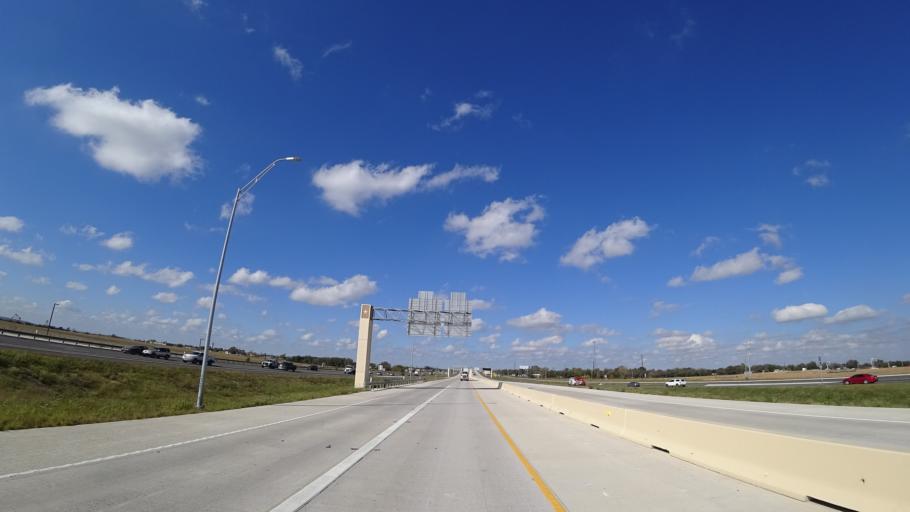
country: US
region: Texas
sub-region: Travis County
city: Hornsby Bend
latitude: 30.1995
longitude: -97.6329
